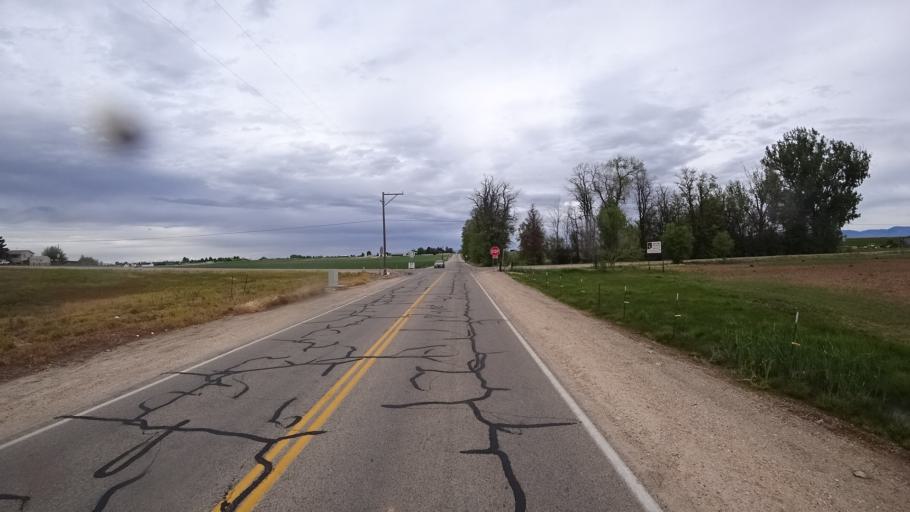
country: US
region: Idaho
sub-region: Ada County
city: Meridian
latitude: 43.5603
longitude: -116.4140
